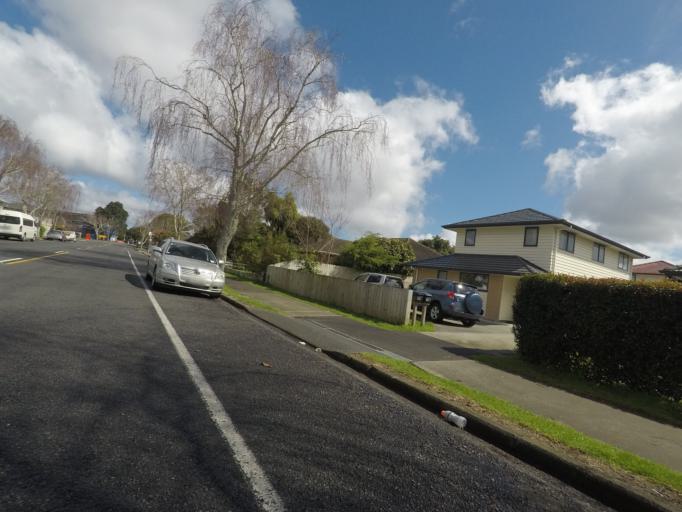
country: NZ
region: Auckland
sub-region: Auckland
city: Rosebank
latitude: -36.8895
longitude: 174.6801
